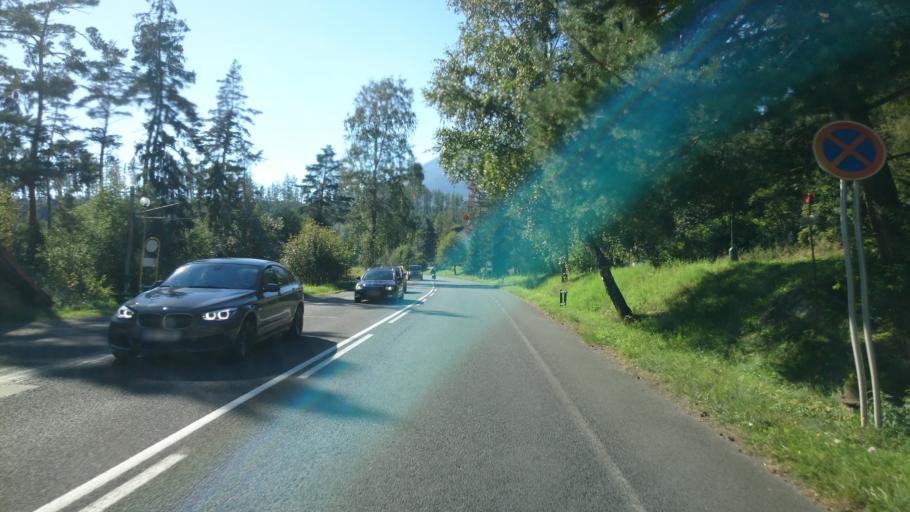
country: SK
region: Presovsky
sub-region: Okres Poprad
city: Vysoke Tatry
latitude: 49.1502
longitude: 20.2568
